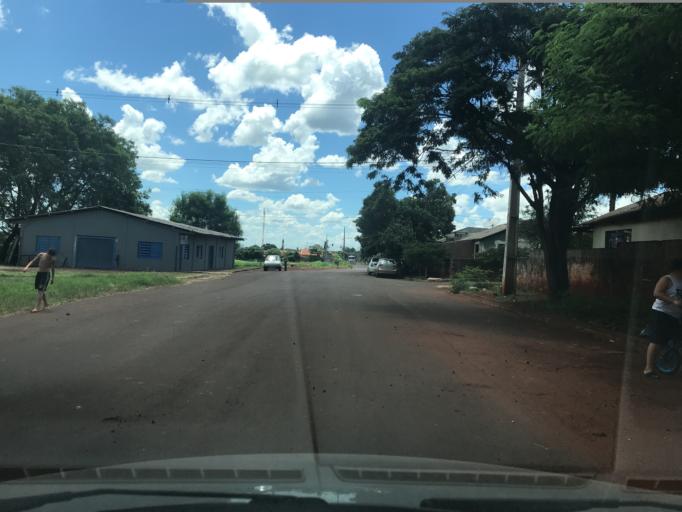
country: BR
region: Parana
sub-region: Palotina
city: Palotina
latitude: -24.2692
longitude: -53.8475
